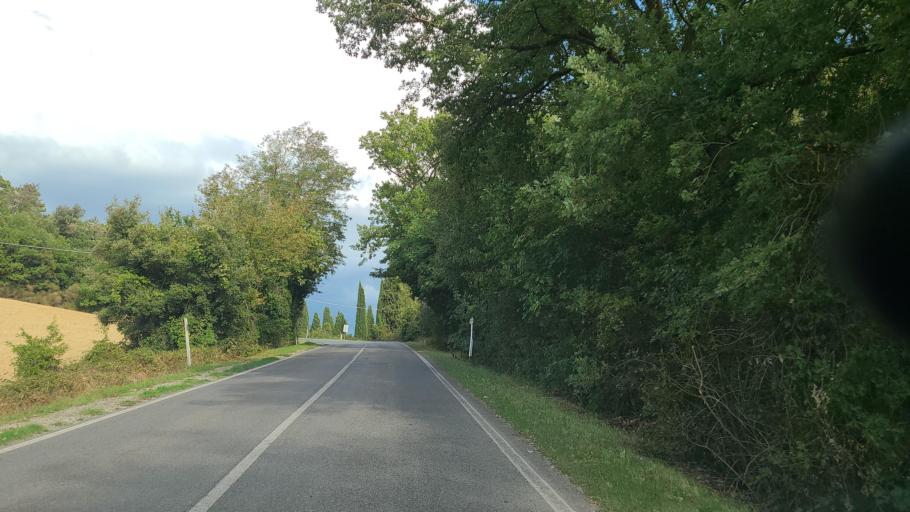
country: IT
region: Tuscany
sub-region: Province of Florence
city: Gambassi Terme
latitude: 43.4863
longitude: 10.9742
